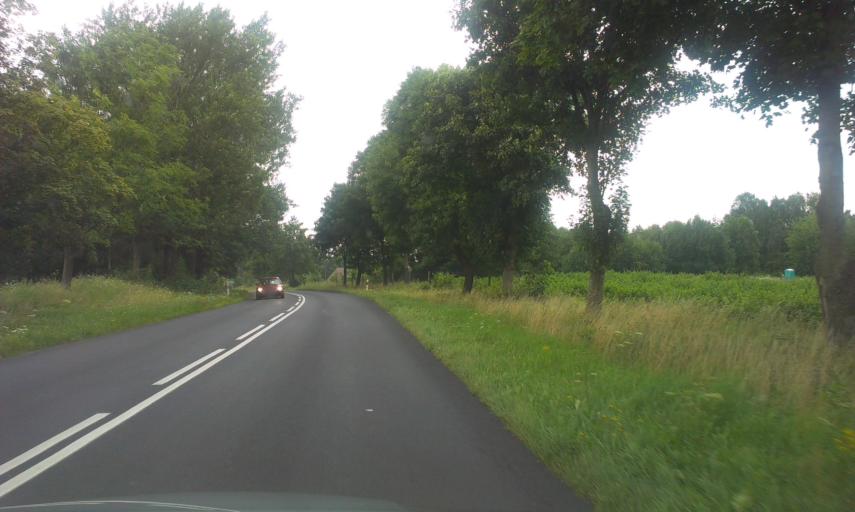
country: PL
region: West Pomeranian Voivodeship
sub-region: Powiat swidwinski
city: Polczyn-Zdroj
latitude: 53.8514
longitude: 16.0744
